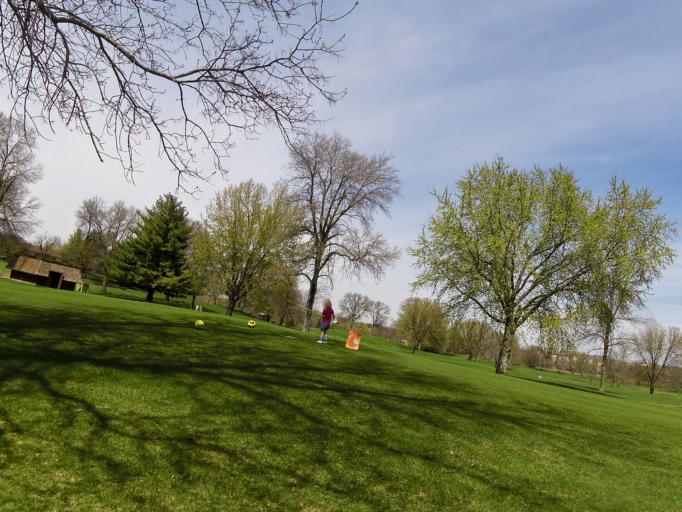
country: US
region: Minnesota
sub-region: Scott County
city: Savage
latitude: 44.8189
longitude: -93.3563
